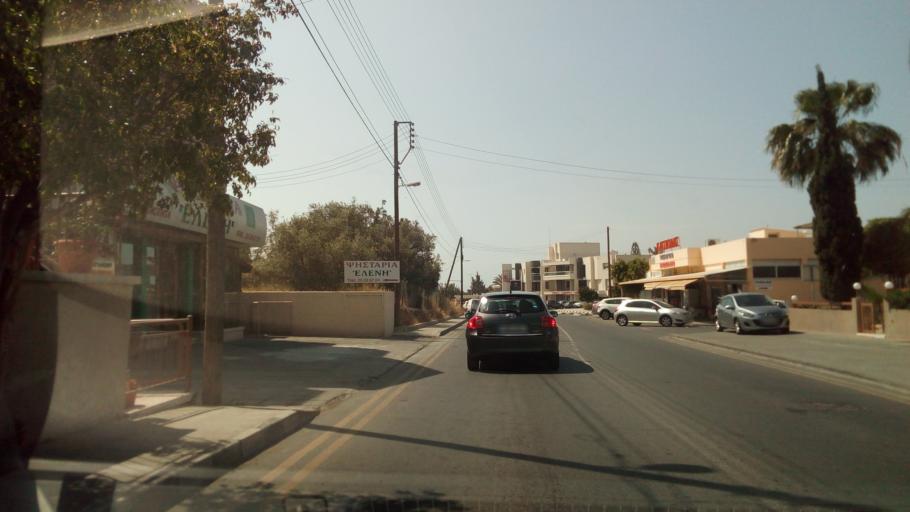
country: CY
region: Limassol
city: Limassol
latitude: 34.7092
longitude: 33.0245
